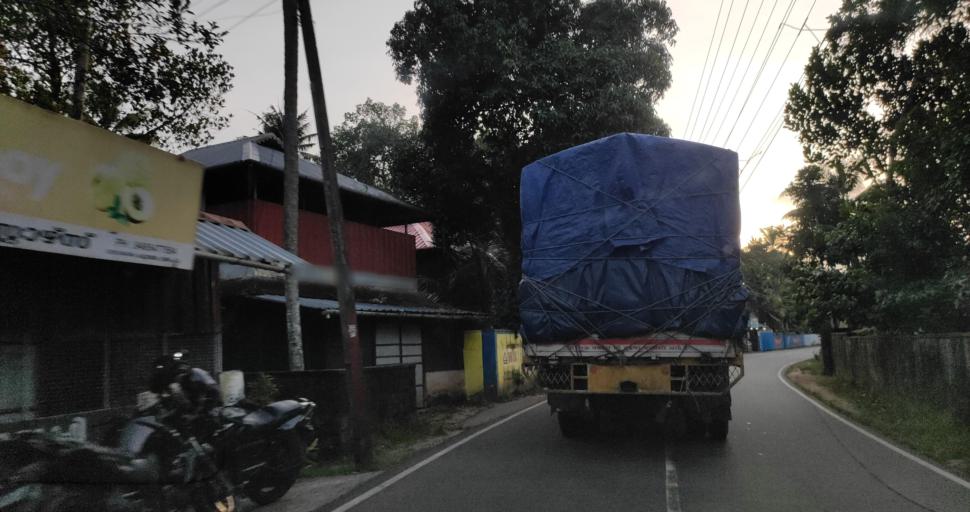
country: IN
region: Kerala
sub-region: Alappuzha
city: Shertallai
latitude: 9.6400
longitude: 76.3477
